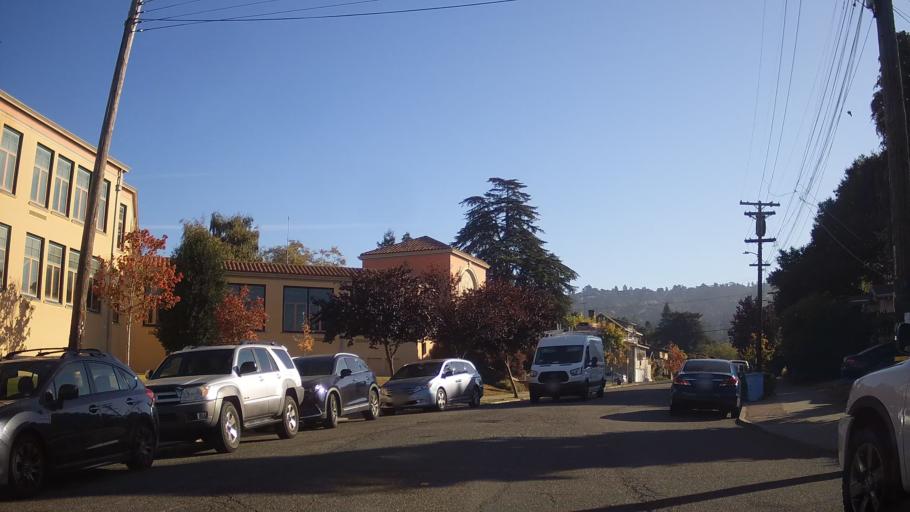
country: US
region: California
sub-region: Alameda County
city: Berkeley
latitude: 37.8810
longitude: -122.2773
